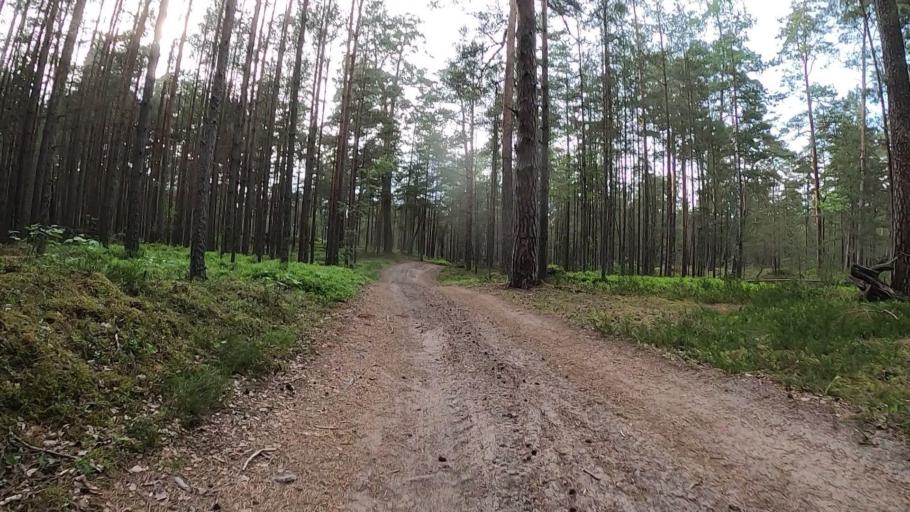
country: LV
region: Riga
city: Jaunciems
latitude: 57.0748
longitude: 24.1316
